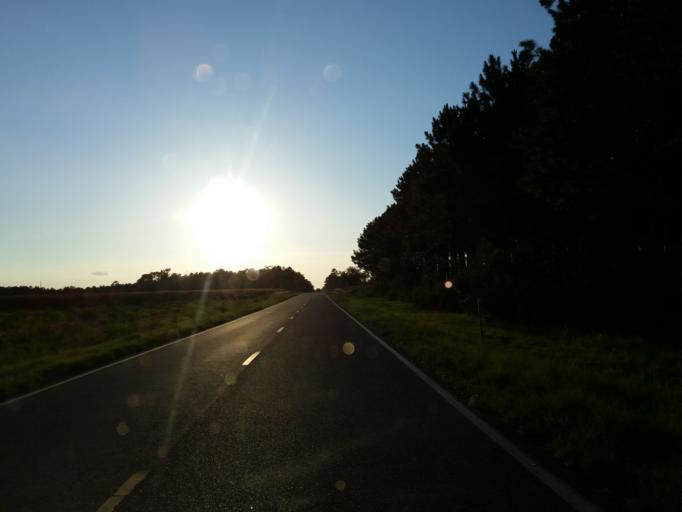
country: US
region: Georgia
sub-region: Lanier County
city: Lakeland
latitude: 31.1649
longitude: -83.0914
